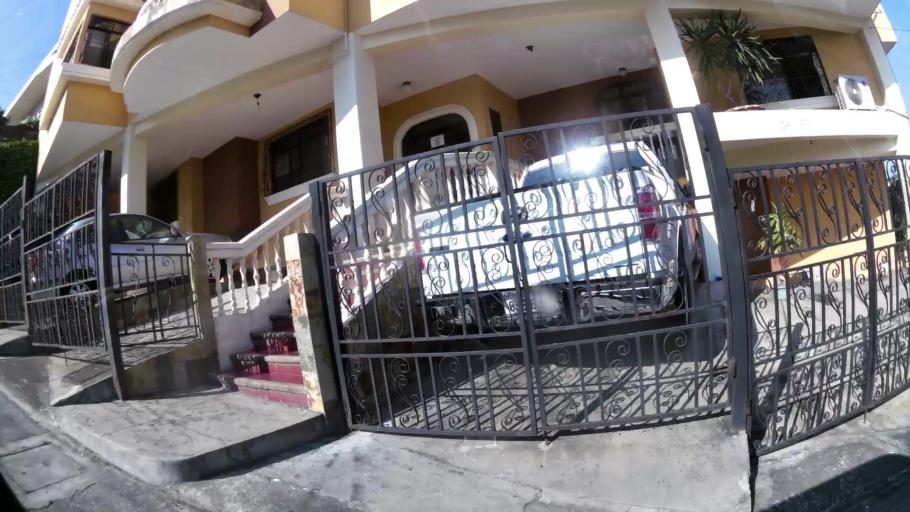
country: EC
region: Guayas
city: Guayaquil
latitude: -2.1633
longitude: -79.9066
